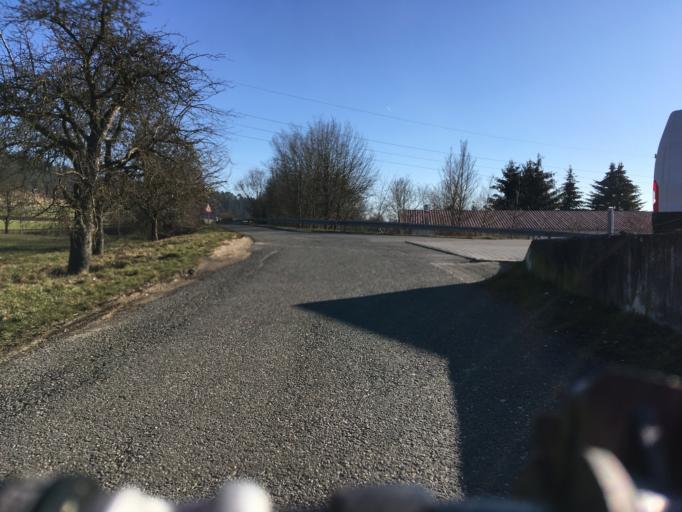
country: DE
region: Baden-Wuerttemberg
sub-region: Freiburg Region
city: Hilzingen
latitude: 47.7613
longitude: 8.7926
